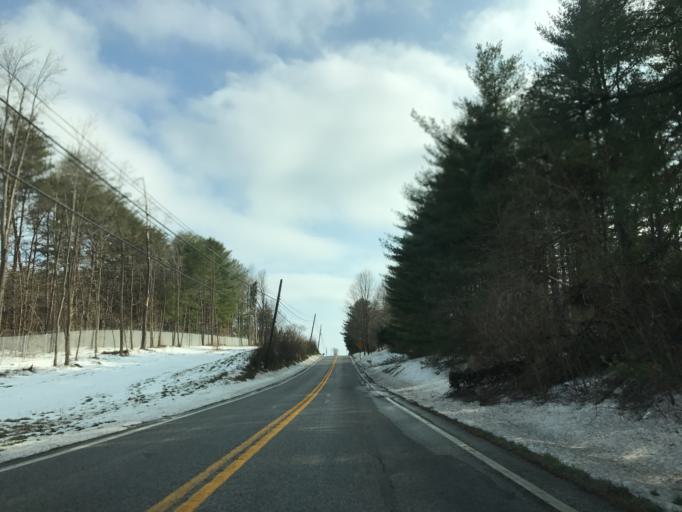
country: US
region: Maryland
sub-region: Harford County
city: South Bel Air
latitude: 39.5944
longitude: -76.2593
